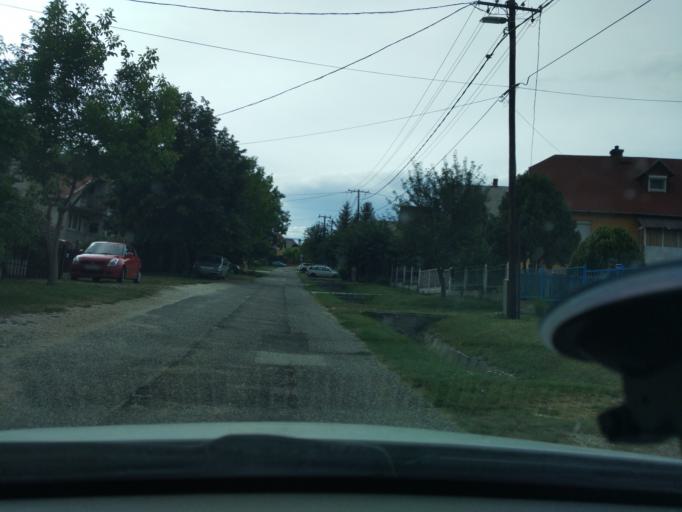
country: HU
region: Veszprem
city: Varpalota
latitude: 47.2018
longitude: 18.1846
